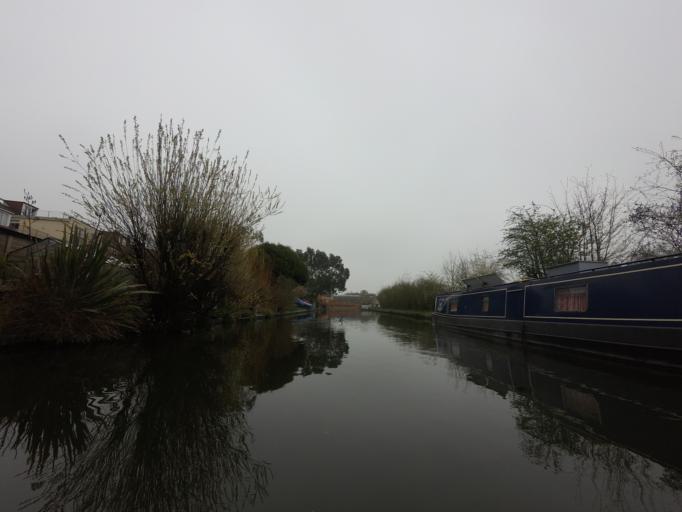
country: GB
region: England
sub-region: Hertfordshire
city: Hemel Hempstead
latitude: 51.7394
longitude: -0.4674
